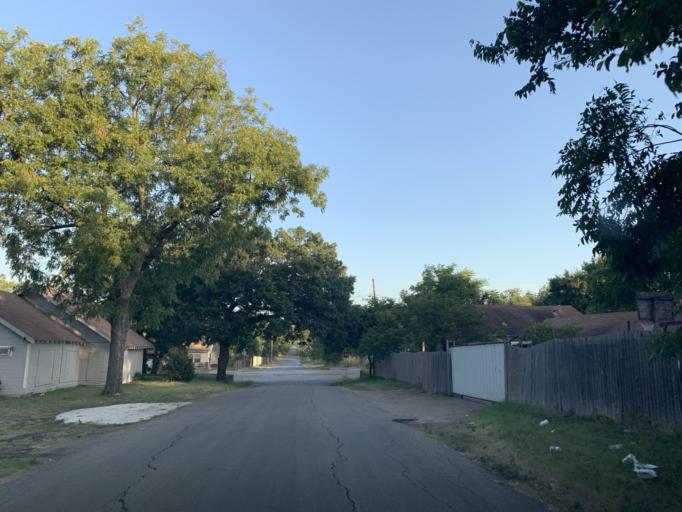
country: US
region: Texas
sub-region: Dallas County
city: Dallas
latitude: 32.7013
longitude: -96.8079
